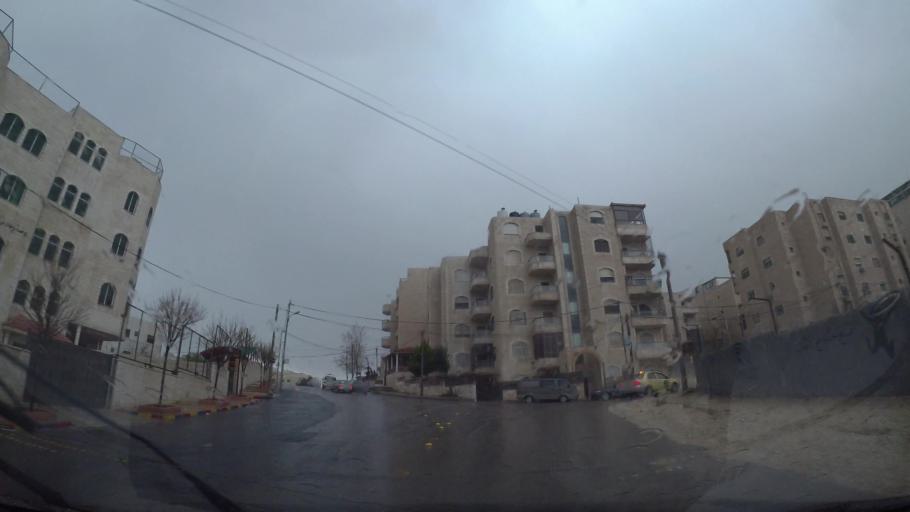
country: JO
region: Amman
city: Amman
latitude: 32.0039
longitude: 35.9544
